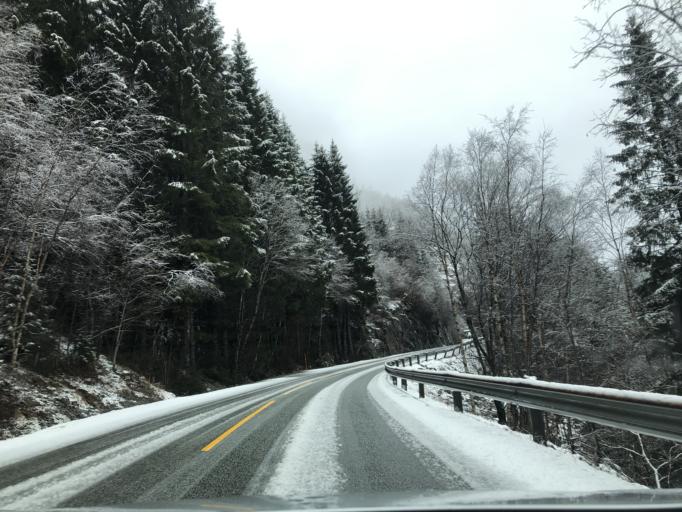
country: NO
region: Rogaland
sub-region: Sauda
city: Sauda
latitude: 59.5282
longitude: 6.5923
